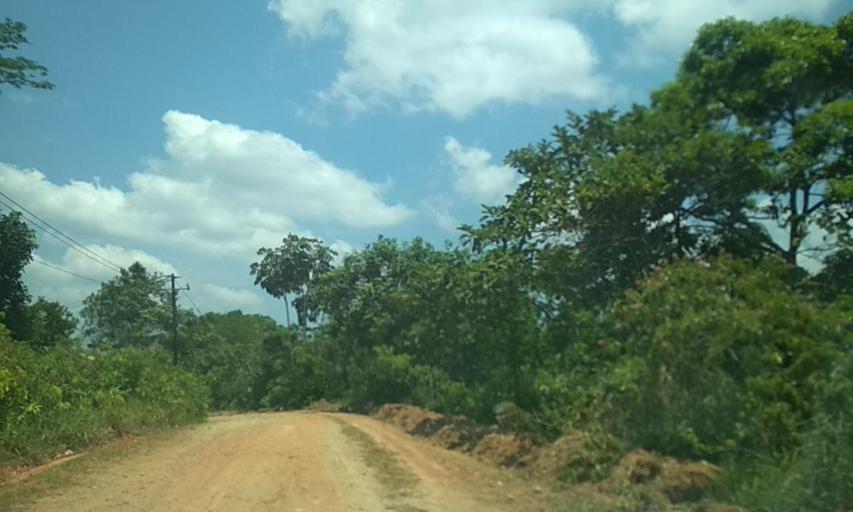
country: MX
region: Chiapas
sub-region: Tecpatan
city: Raudales Malpaso
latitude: 17.3933
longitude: -93.7367
